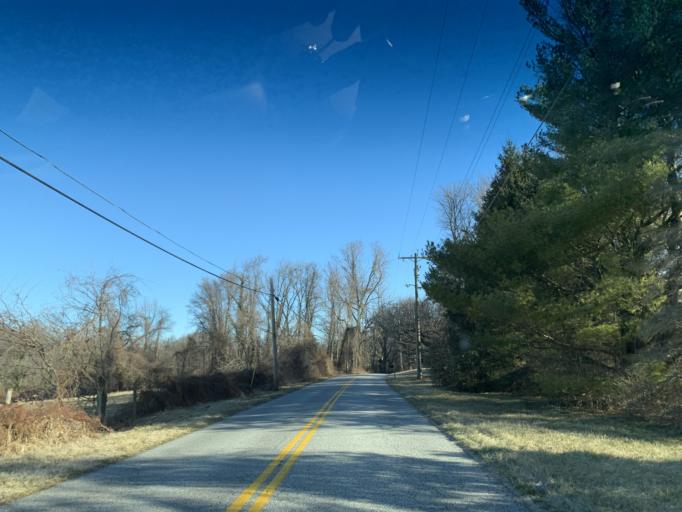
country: US
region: Maryland
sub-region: Harford County
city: Riverside
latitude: 39.5639
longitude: -76.2428
